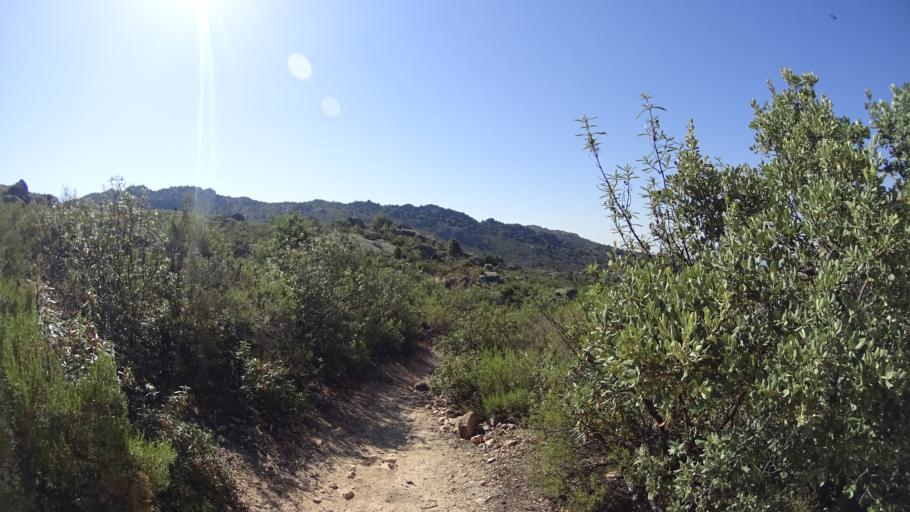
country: ES
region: Madrid
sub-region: Provincia de Madrid
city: Hoyo de Manzanares
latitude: 40.6413
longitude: -3.9355
